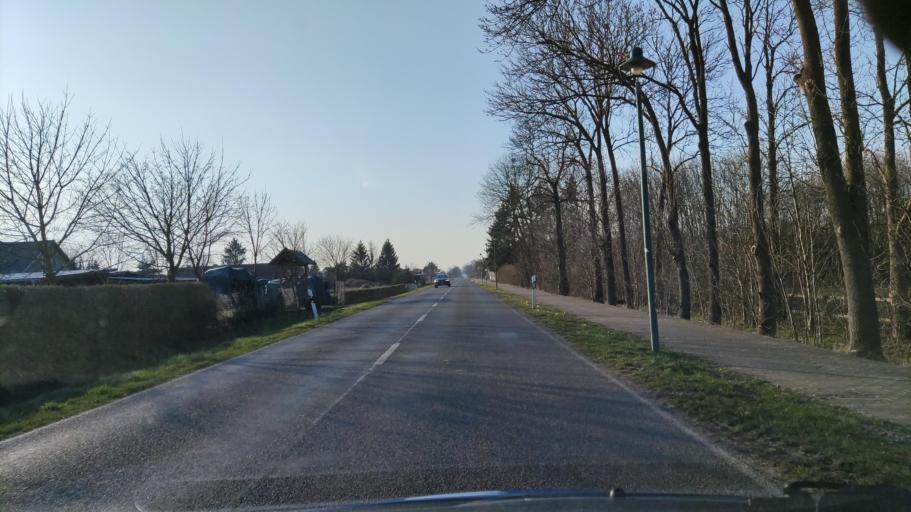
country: DE
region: Brandenburg
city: Cumlosen
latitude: 52.9530
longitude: 11.6487
